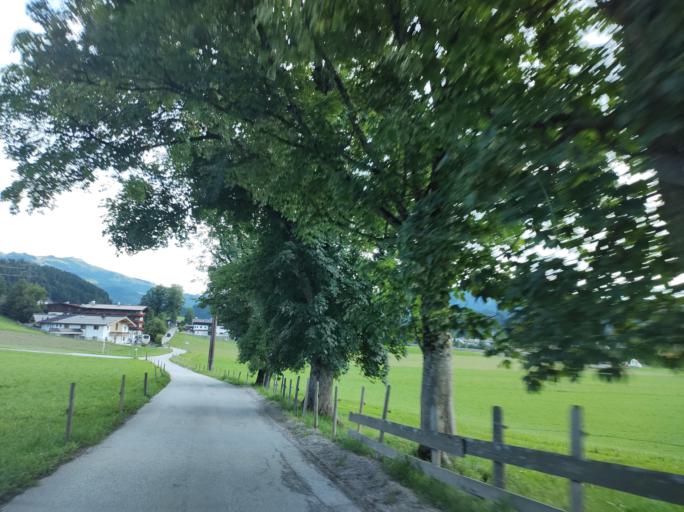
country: AT
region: Tyrol
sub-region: Politischer Bezirk Kitzbuhel
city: Oberndorf in Tirol
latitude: 47.5010
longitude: 12.3975
